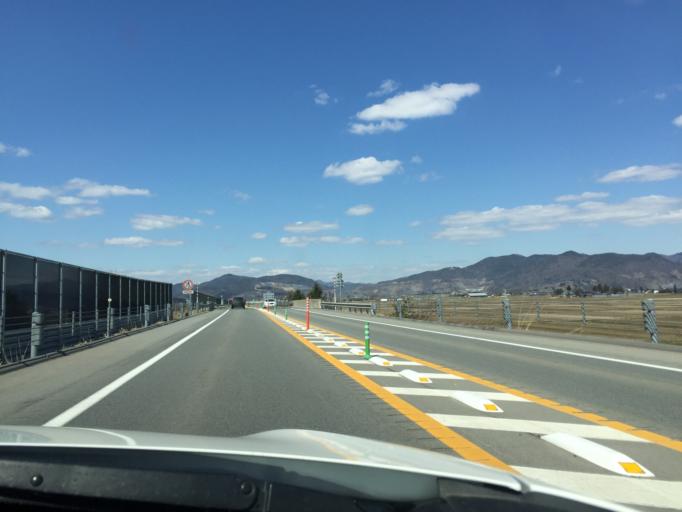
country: JP
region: Yamagata
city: Takahata
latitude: 38.0117
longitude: 140.1570
